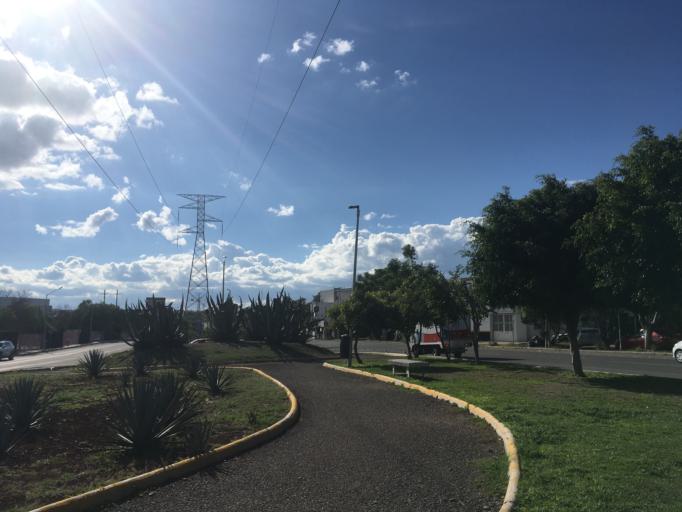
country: MX
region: Queretaro
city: San Jose el Alto
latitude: 20.6221
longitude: -100.3925
